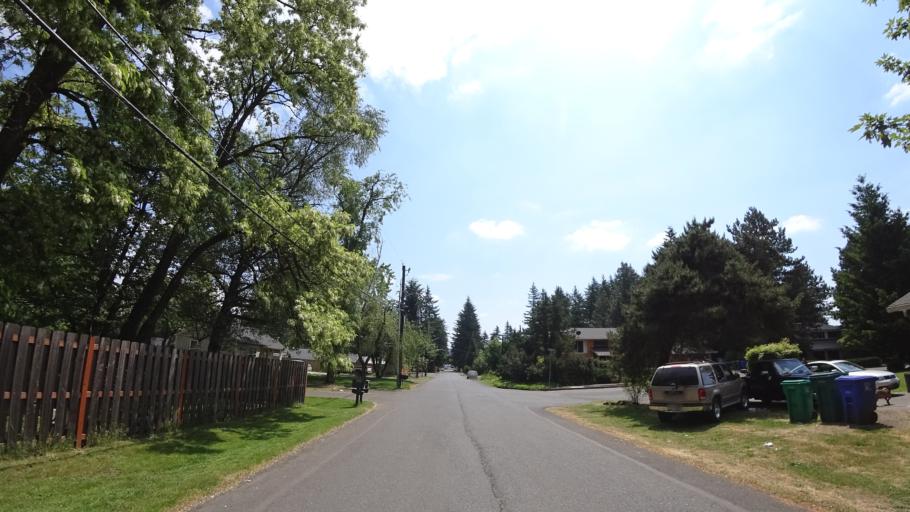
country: US
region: Oregon
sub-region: Multnomah County
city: Lents
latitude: 45.5247
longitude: -122.5080
